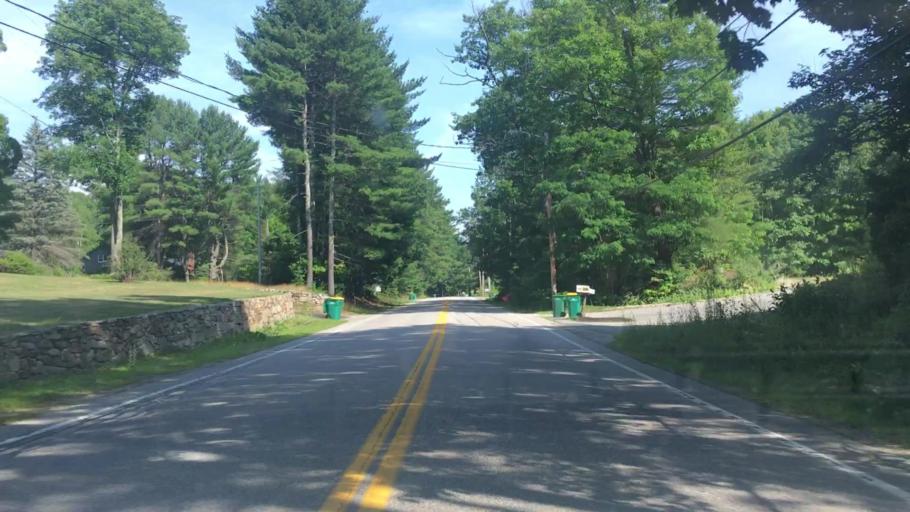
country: US
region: New Hampshire
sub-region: Strafford County
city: Rochester
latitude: 43.2746
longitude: -70.9585
